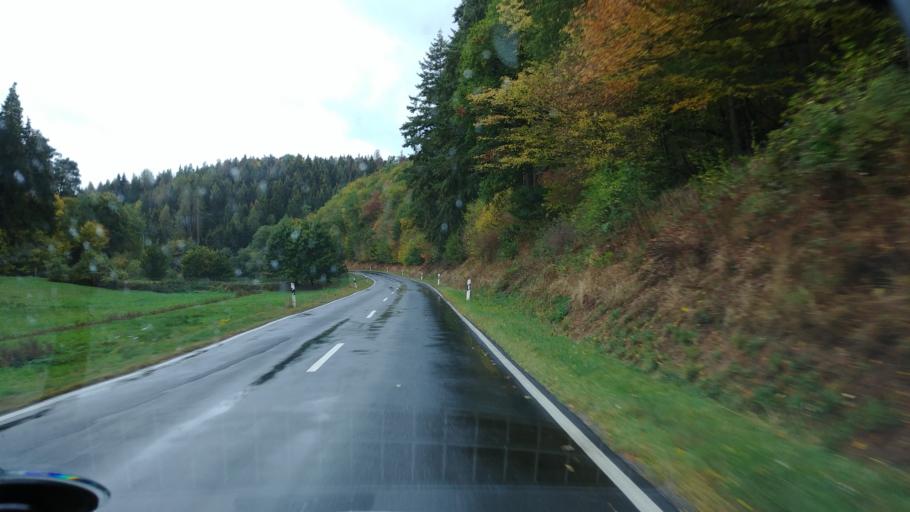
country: DE
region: Hesse
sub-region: Regierungsbezirk Darmstadt
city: Bad Schwalbach
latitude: 50.1465
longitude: 8.0966
